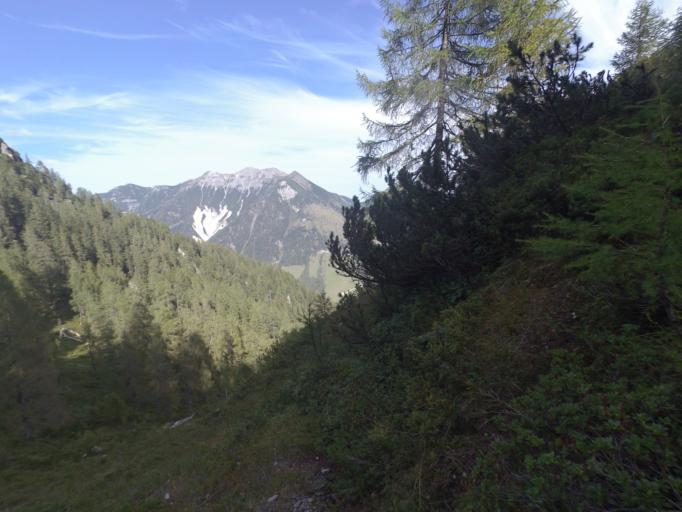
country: AT
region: Salzburg
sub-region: Politischer Bezirk Sankt Johann im Pongau
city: Kleinarl
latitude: 47.2394
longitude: 13.4099
